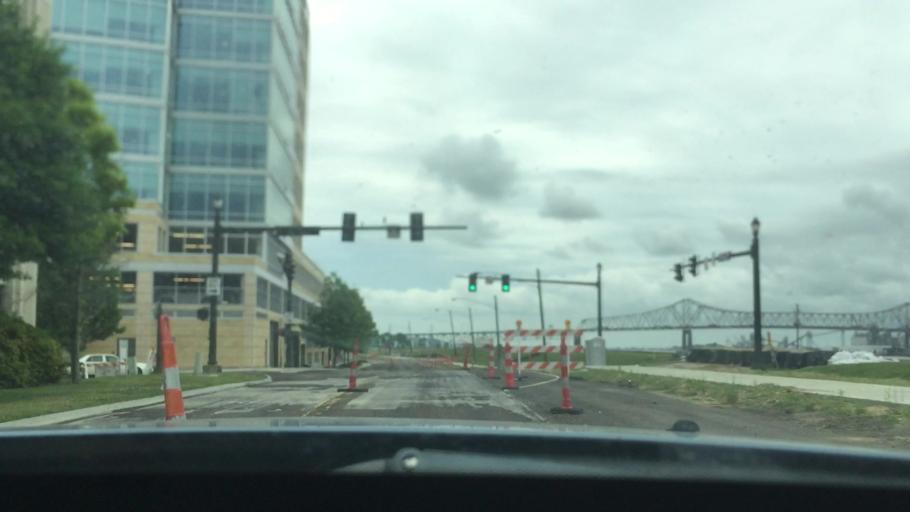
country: US
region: Louisiana
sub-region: West Baton Rouge Parish
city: Port Allen
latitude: 30.4529
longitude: -91.1904
